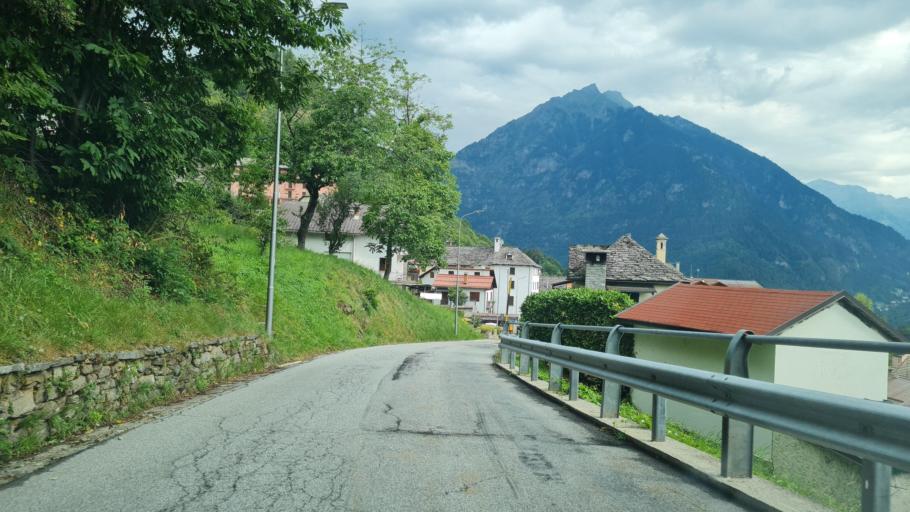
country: IT
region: Piedmont
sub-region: Provincia Verbano-Cusio-Ossola
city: Crodo
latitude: 46.2381
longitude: 8.3127
